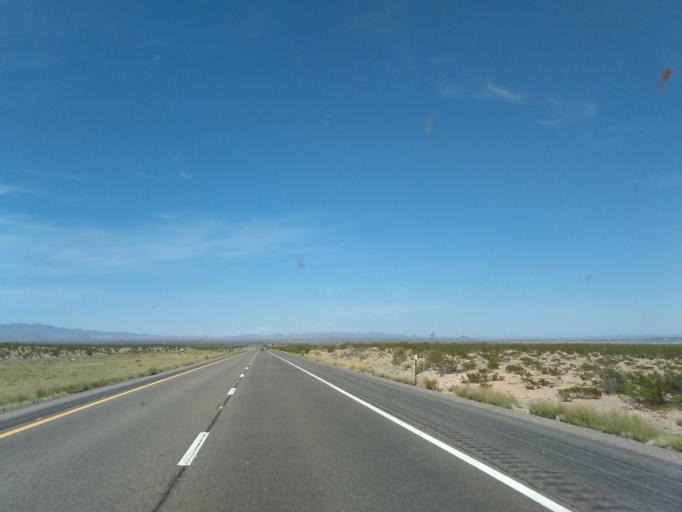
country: US
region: New Mexico
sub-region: Sierra County
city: Elephant Butte
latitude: 33.5817
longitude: -107.1656
